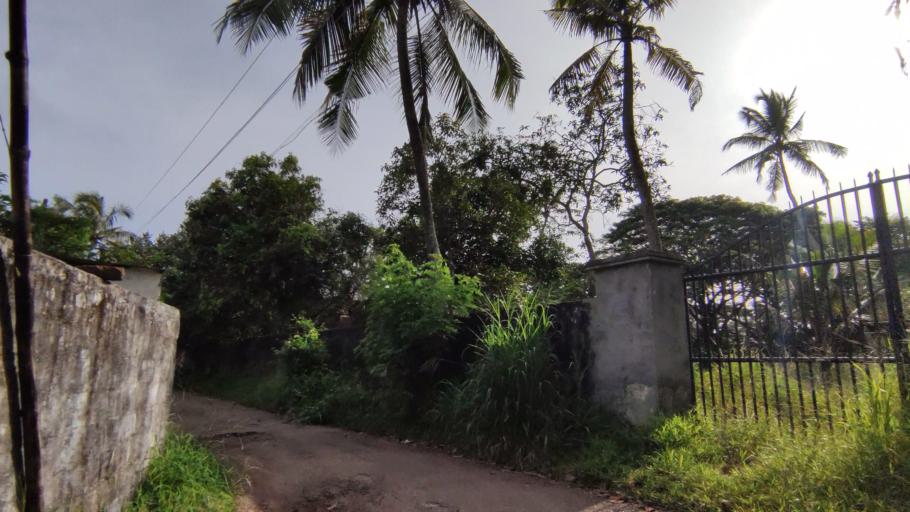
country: IN
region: Kerala
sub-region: Alappuzha
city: Shertallai
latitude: 9.6292
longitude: 76.3343
